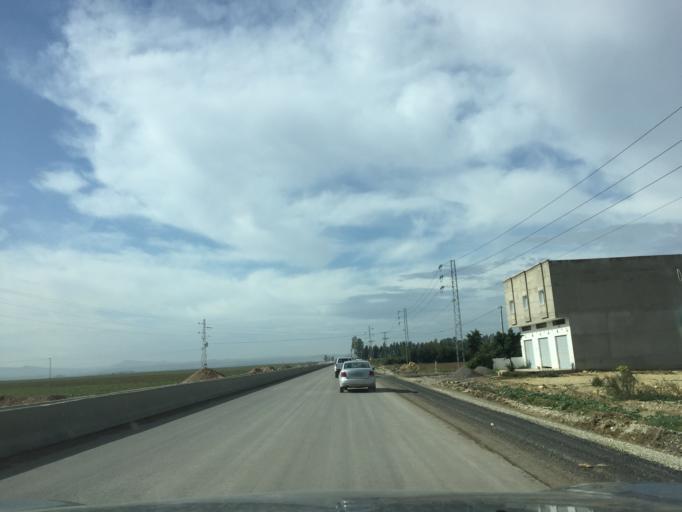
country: TN
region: Zaghwan
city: El Fahs
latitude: 36.3617
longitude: 9.8888
